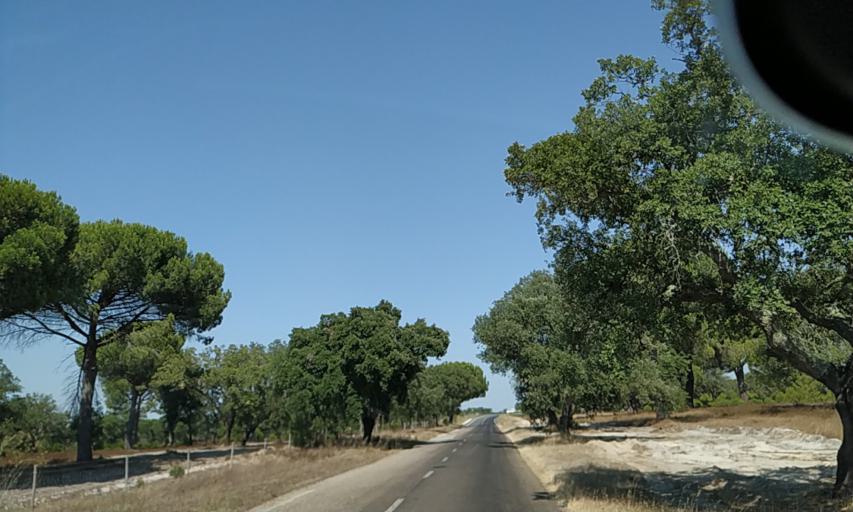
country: PT
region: Santarem
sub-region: Benavente
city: Poceirao
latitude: 38.7425
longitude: -8.6851
